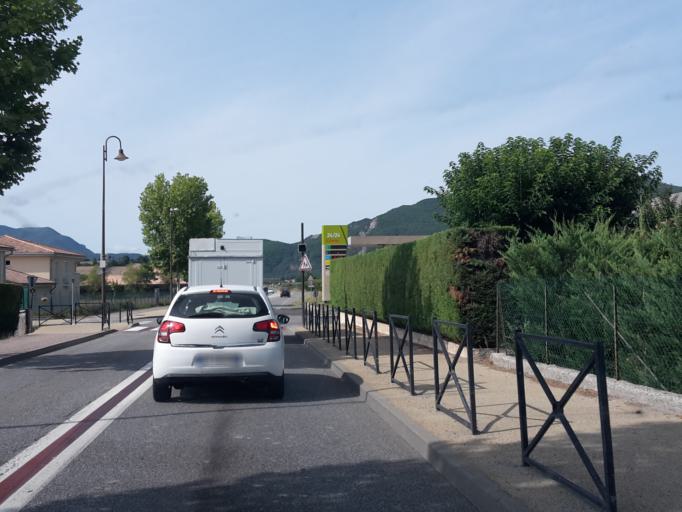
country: FR
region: Provence-Alpes-Cote d'Azur
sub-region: Departement des Hautes-Alpes
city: Tallard
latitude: 44.4587
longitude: 6.0507
